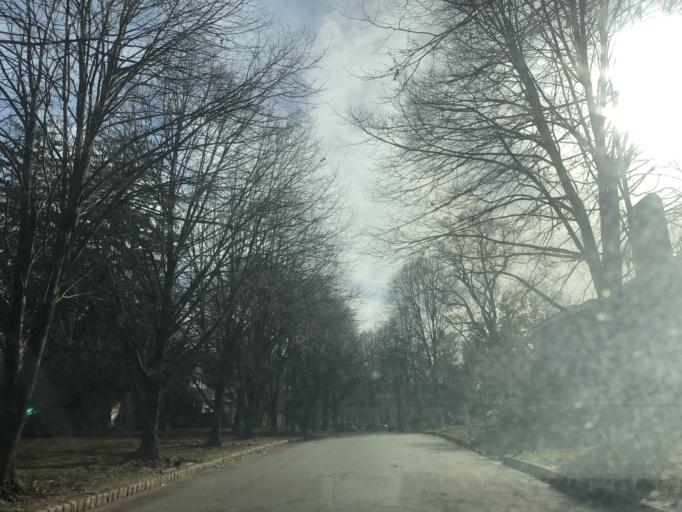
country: US
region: New Jersey
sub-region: Mercer County
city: Princeton
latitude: 40.3568
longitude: -74.6365
